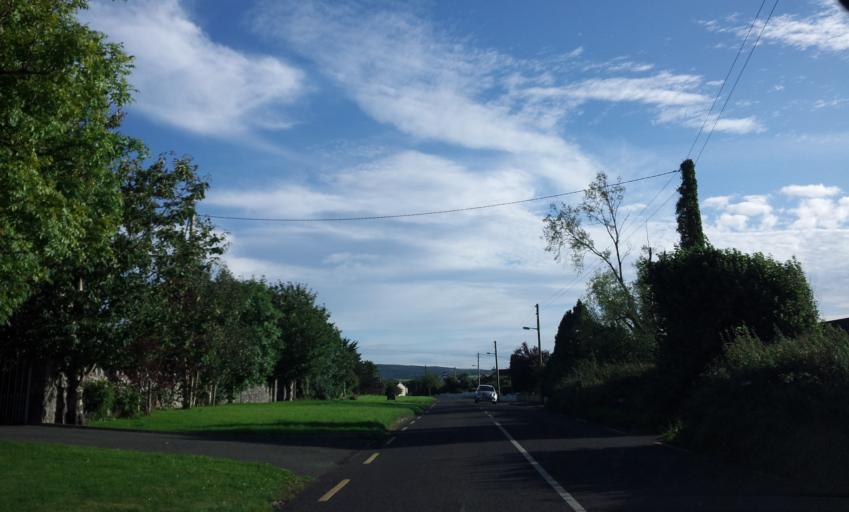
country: IE
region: Munster
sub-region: An Clar
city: Ennis
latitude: 52.9501
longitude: -9.0673
